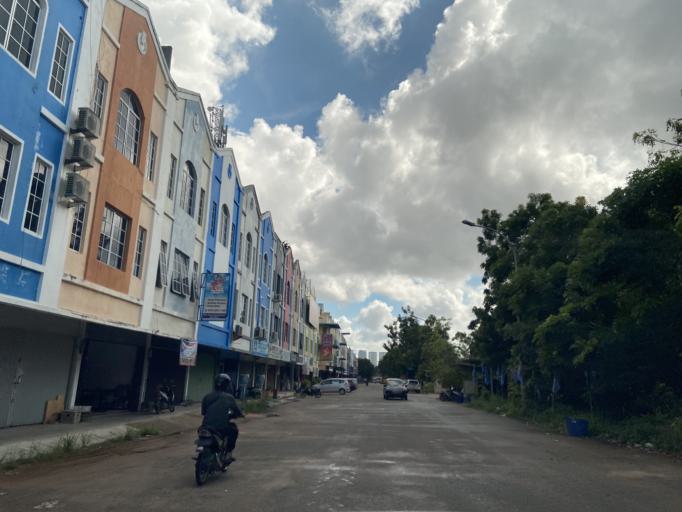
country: SG
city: Singapore
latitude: 1.0937
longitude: 104.0350
